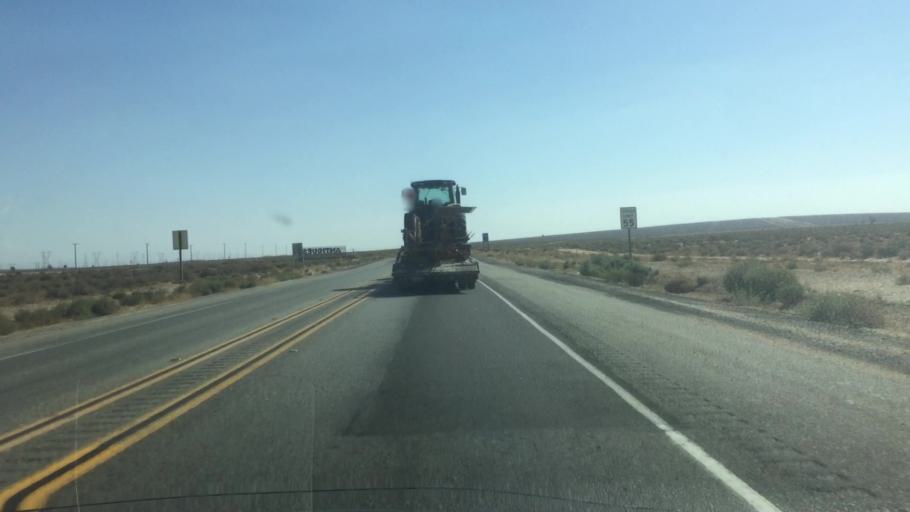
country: US
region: California
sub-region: Kern County
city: Boron
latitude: 34.9913
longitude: -117.5312
